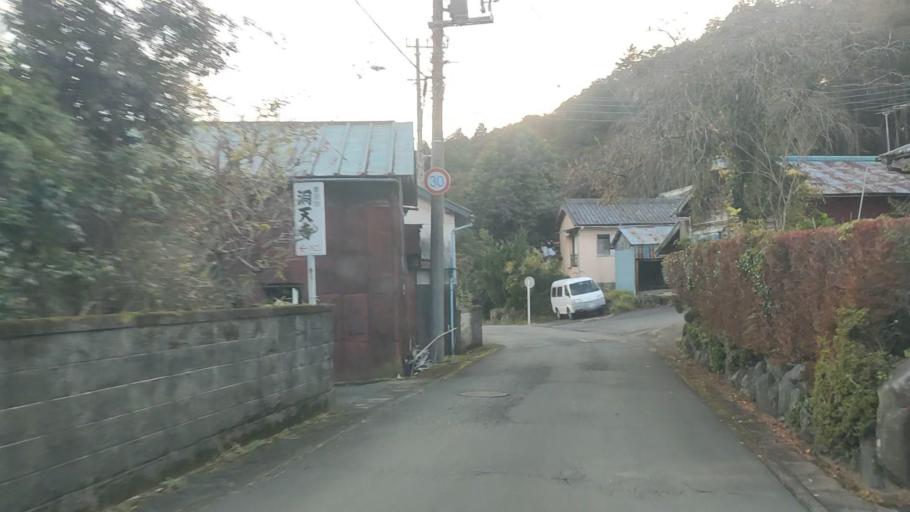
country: JP
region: Kanagawa
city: Yugawara
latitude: 35.1253
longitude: 139.0156
